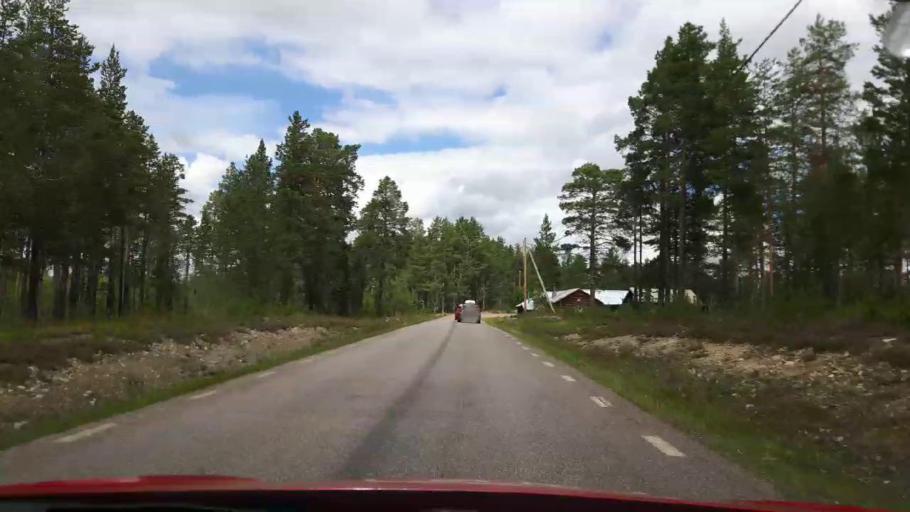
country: NO
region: Hedmark
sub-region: Trysil
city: Innbygda
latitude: 61.8314
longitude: 12.9524
